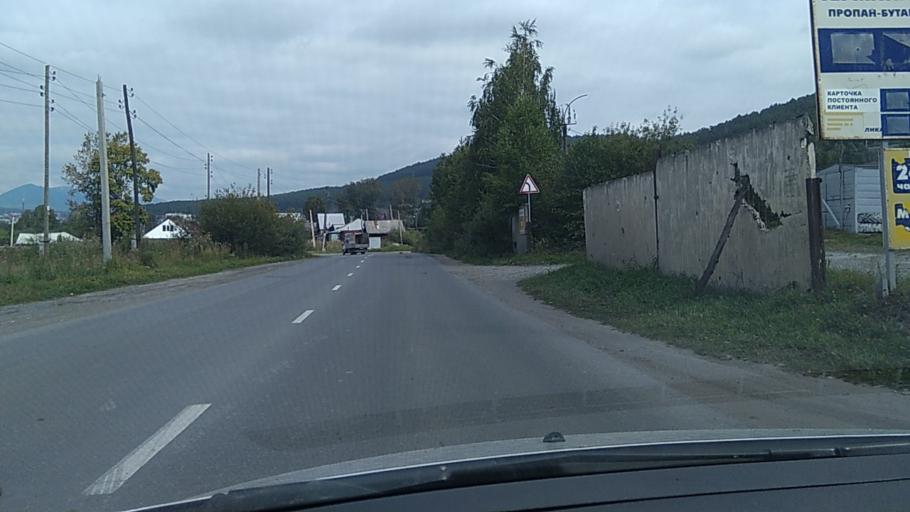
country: RU
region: Chelyabinsk
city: Zlatoust
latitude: 55.1701
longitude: 59.7063
